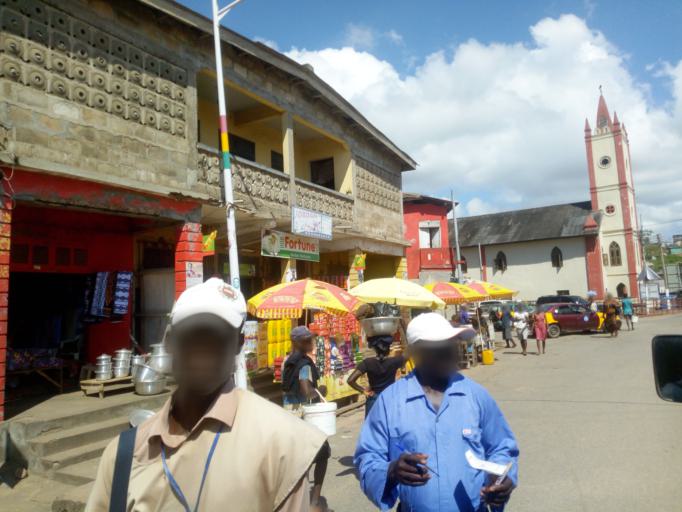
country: GH
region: Central
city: Elmina
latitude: 5.0852
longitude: -1.3497
